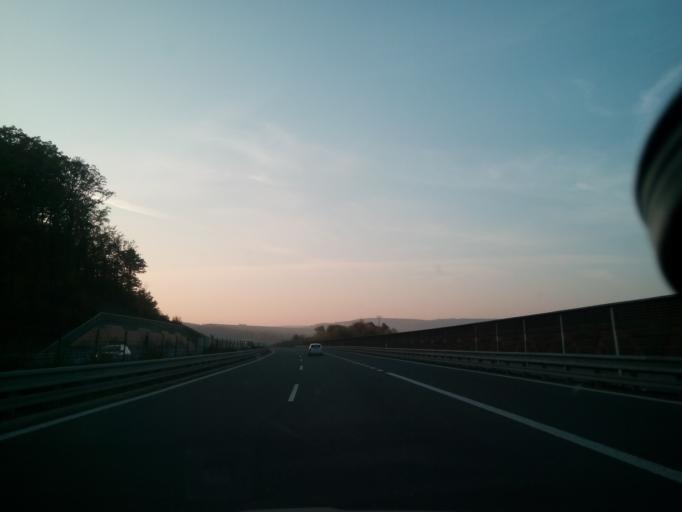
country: SK
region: Presovsky
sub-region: Okres Presov
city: Presov
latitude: 49.0017
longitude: 21.1829
